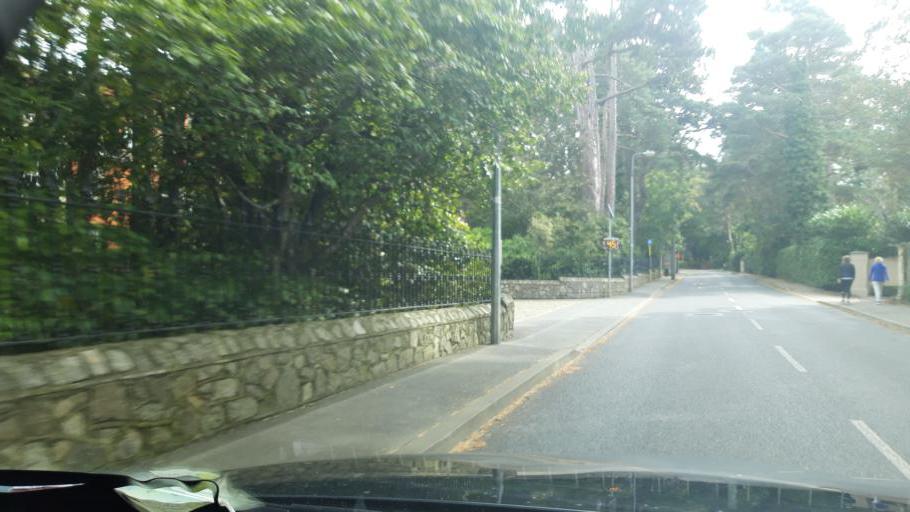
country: IE
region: Leinster
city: Foxrock
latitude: 53.2642
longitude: -6.1819
